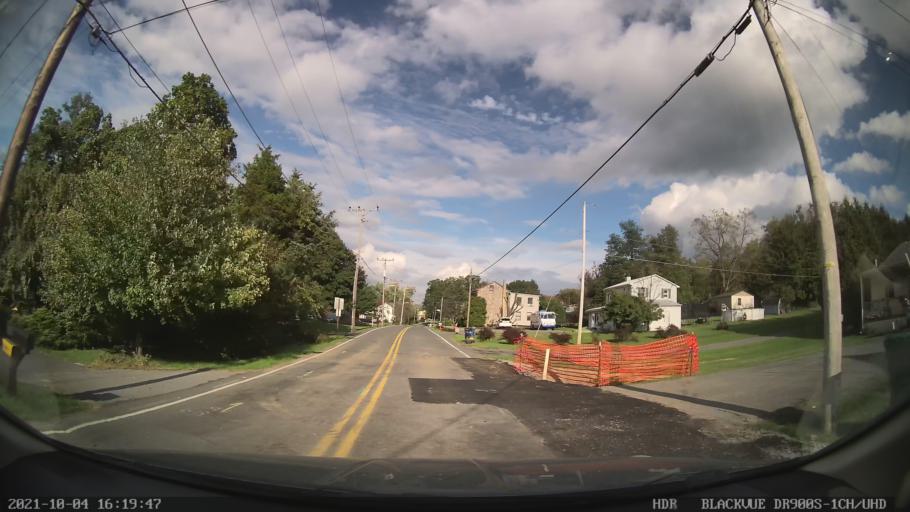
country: US
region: Pennsylvania
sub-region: Berks County
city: Blandon
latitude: 40.4347
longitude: -75.8920
